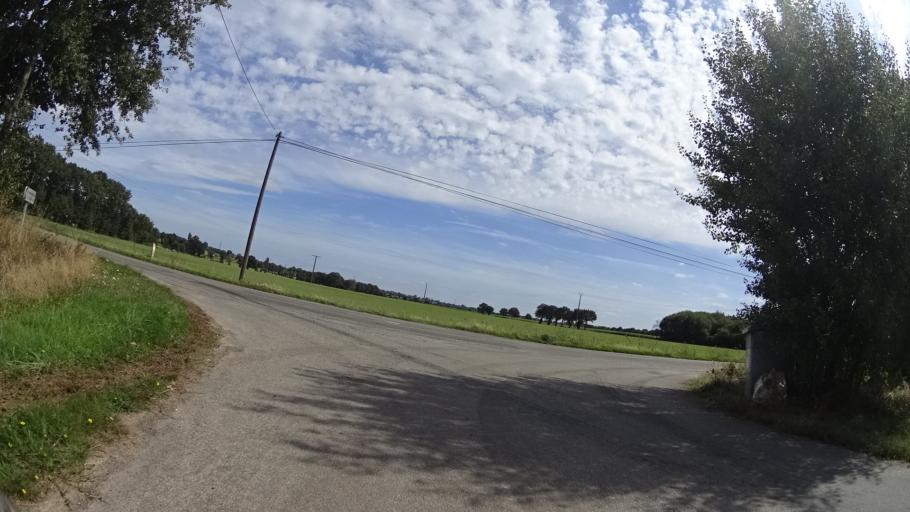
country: FR
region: Brittany
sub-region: Departement d'Ille-et-Vilaine
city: La Meziere
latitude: 48.2284
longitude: -1.7429
